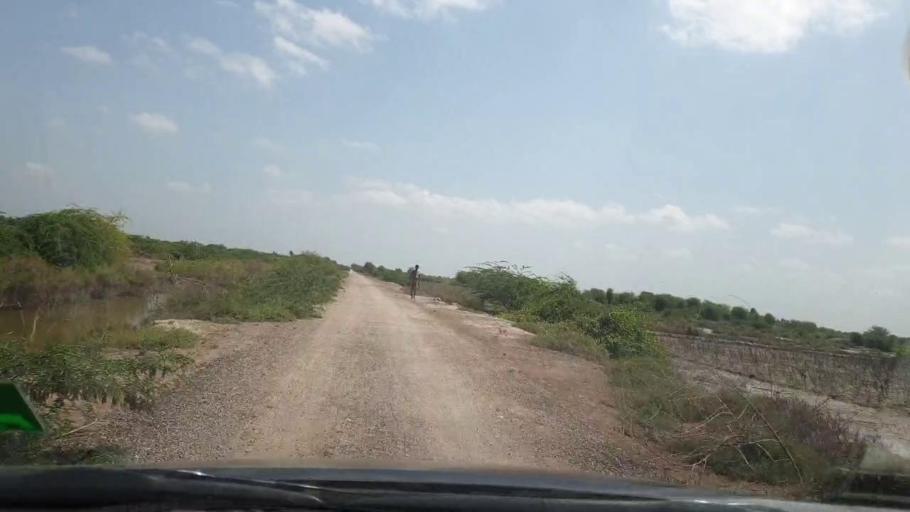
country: PK
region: Sindh
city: Tando Bago
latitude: 24.8611
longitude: 69.1005
